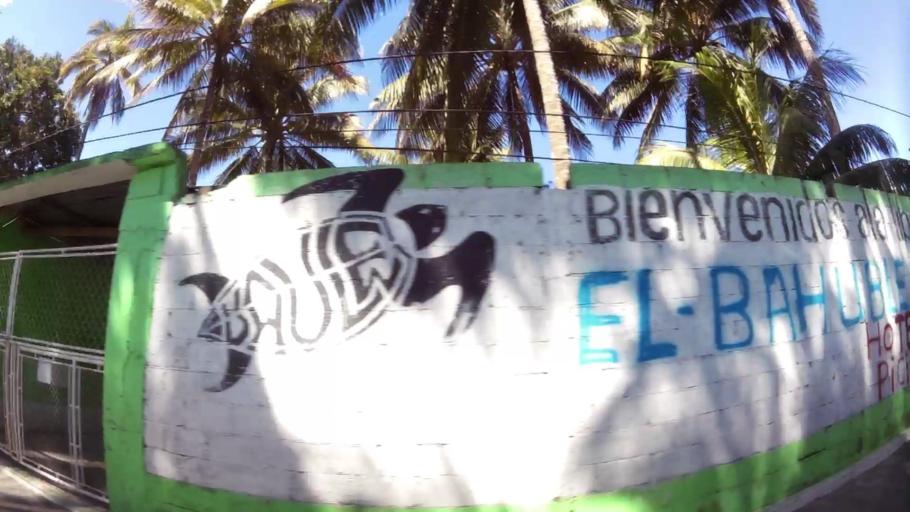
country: GT
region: Escuintla
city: Iztapa
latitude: 13.9309
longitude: -90.7109
